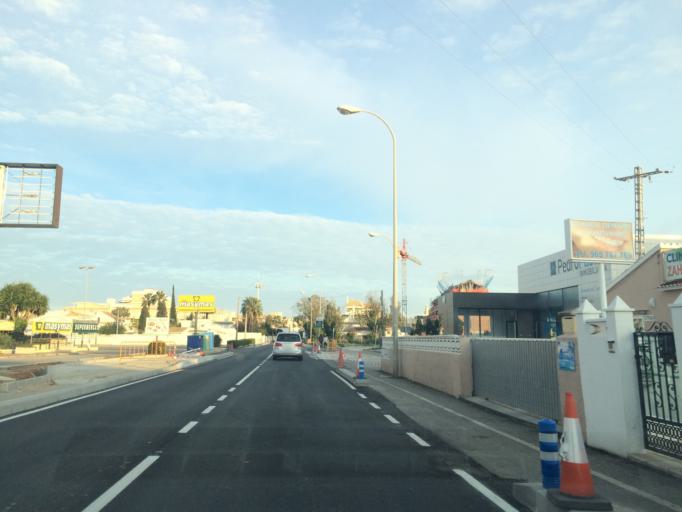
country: ES
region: Valencia
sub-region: Provincia de Alicante
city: els Poblets
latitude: 38.8585
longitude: 0.0589
